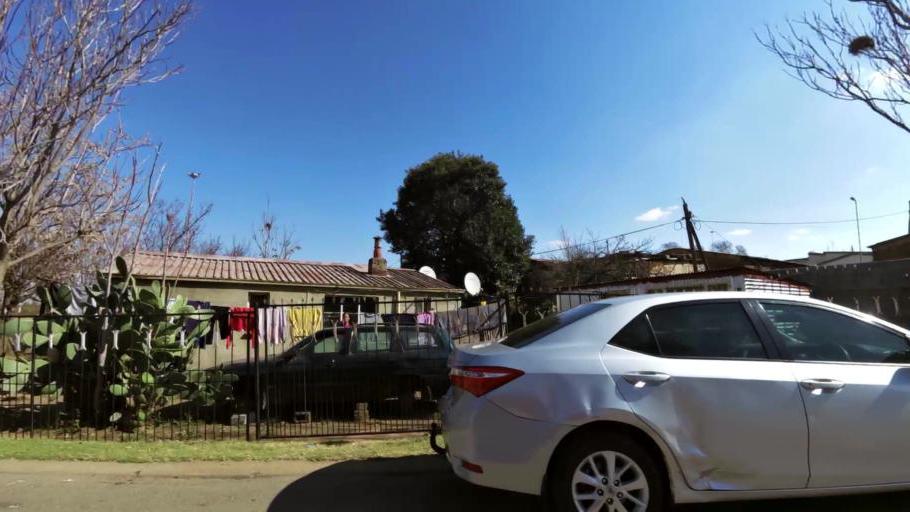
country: ZA
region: Gauteng
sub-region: City of Johannesburg Metropolitan Municipality
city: Soweto
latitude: -26.2451
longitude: 27.9067
